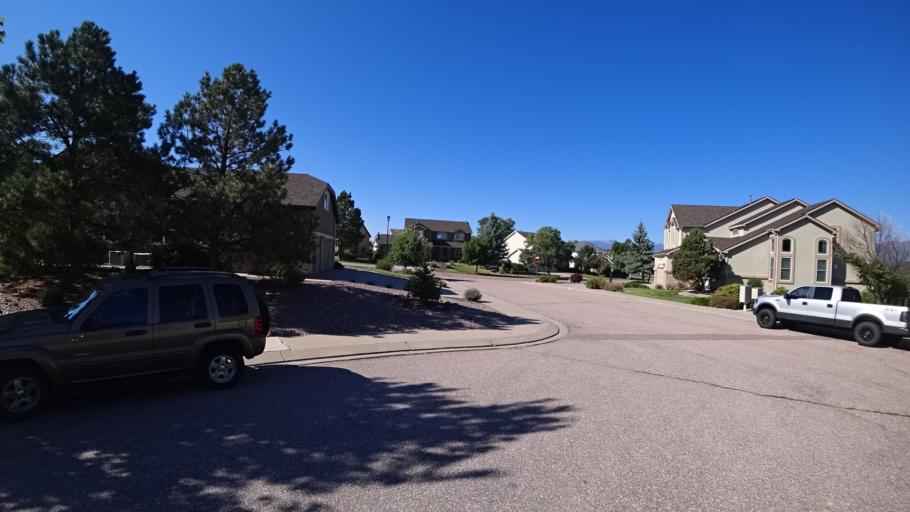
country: US
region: Colorado
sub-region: El Paso County
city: Gleneagle
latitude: 38.9787
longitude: -104.7809
